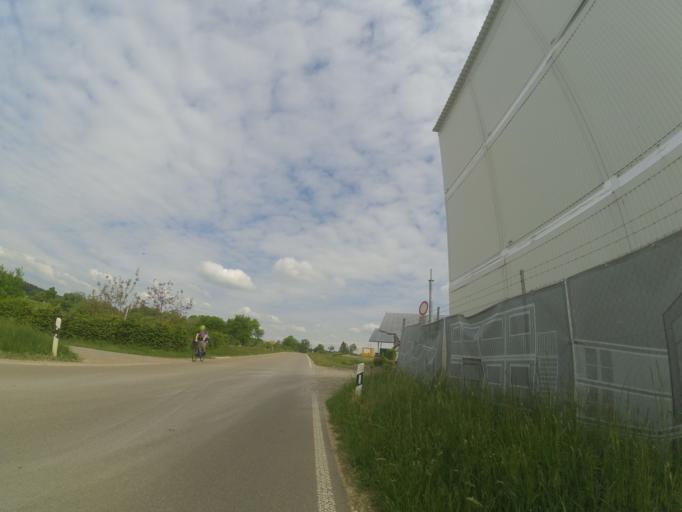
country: DE
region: Baden-Wuerttemberg
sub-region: Tuebingen Region
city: Blaubeuren
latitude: 48.4427
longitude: 9.8150
